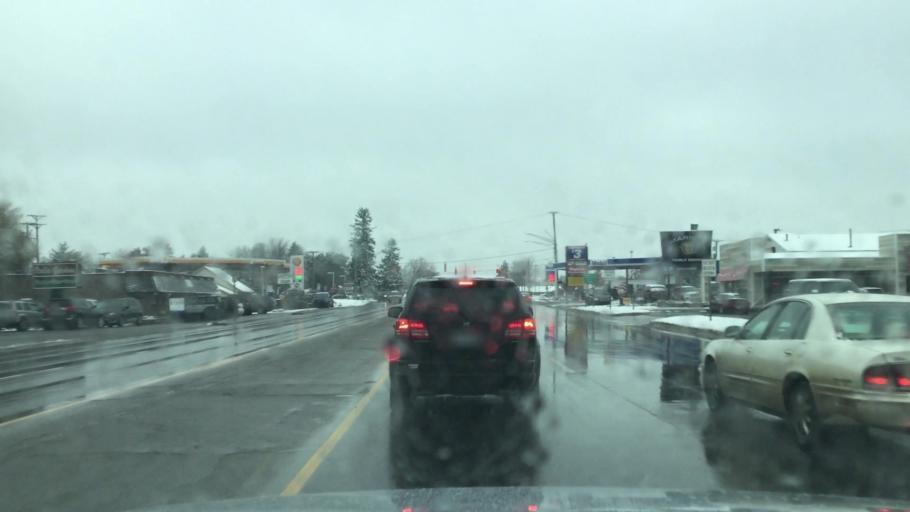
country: US
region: Michigan
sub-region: Oakland County
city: Oxford
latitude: 42.8092
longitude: -83.2506
